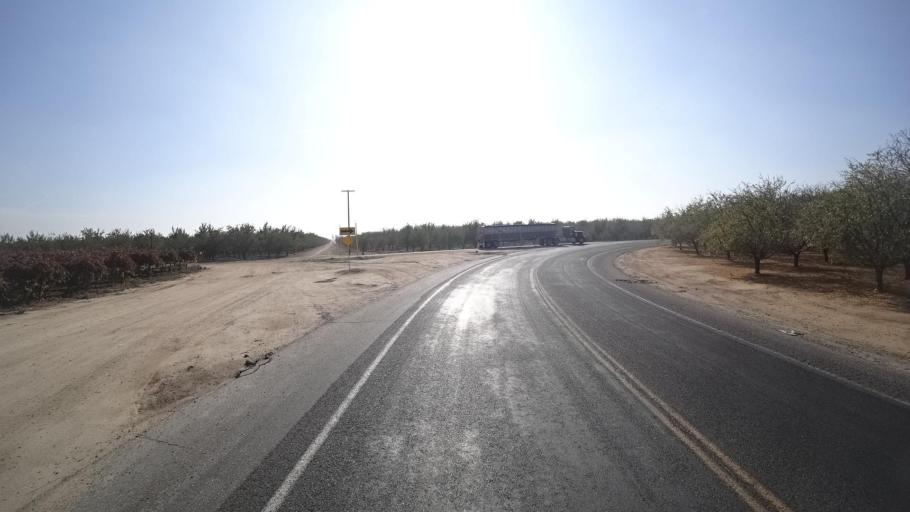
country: US
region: California
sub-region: Kern County
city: McFarland
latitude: 35.6459
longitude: -119.1957
